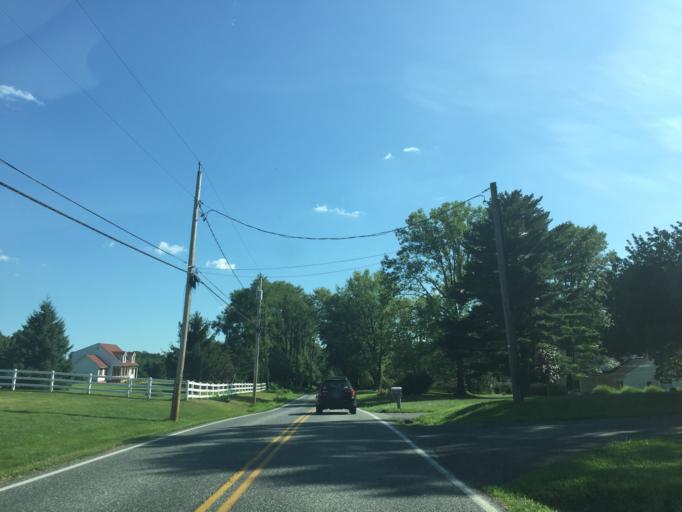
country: US
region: Maryland
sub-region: Harford County
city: Pleasant Hills
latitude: 39.4705
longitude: -76.3812
